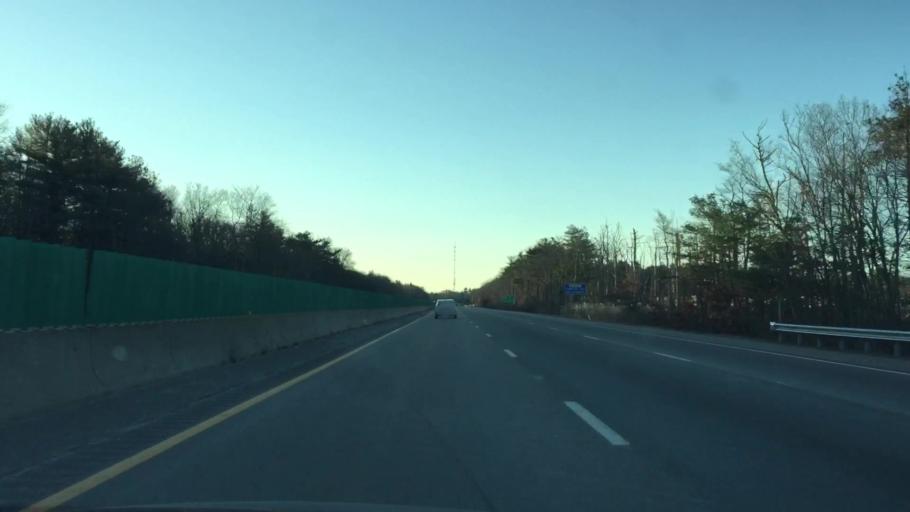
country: US
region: Massachusetts
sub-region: Plymouth County
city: West Bridgewater
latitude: 42.0316
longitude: -71.0515
